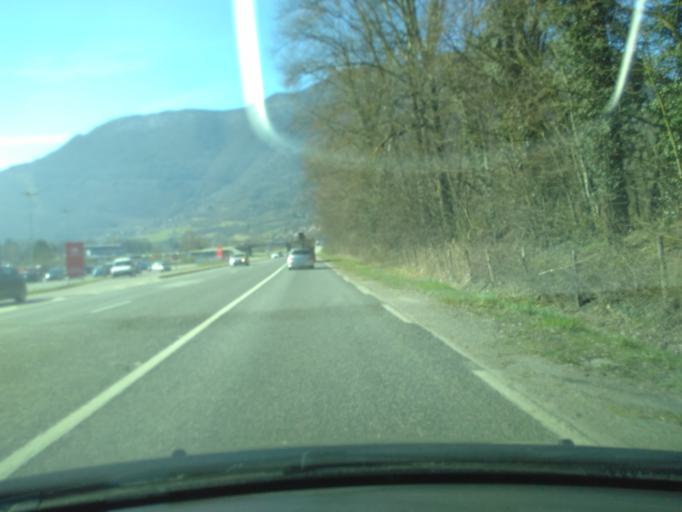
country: FR
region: Rhone-Alpes
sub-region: Departement de l'Isere
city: Vizille
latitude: 45.0729
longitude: 5.7645
